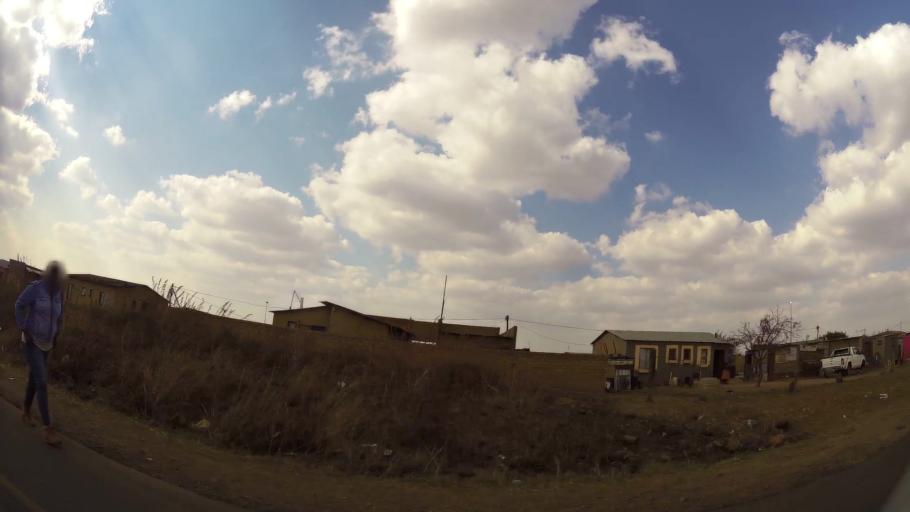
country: ZA
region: Mpumalanga
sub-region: Nkangala District Municipality
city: Delmas
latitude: -26.0970
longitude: 28.6778
